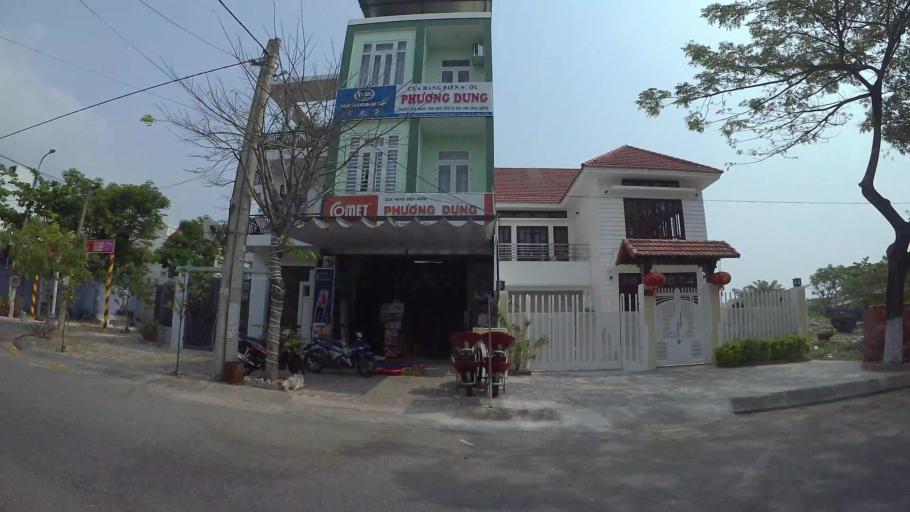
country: VN
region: Da Nang
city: Da Nang
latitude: 16.0942
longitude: 108.2310
